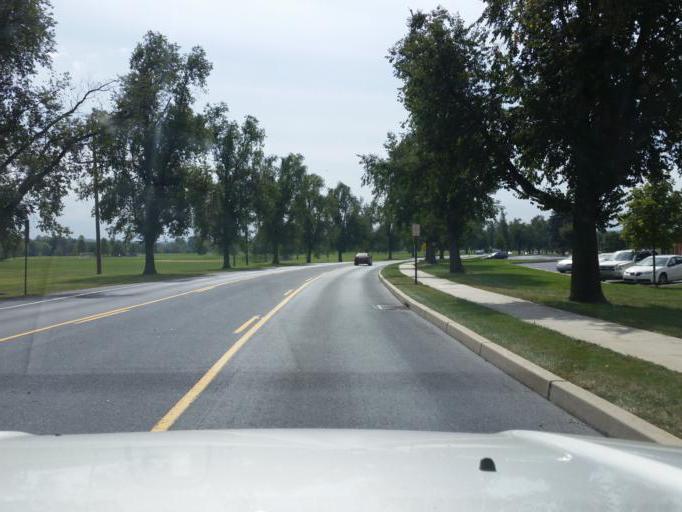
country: US
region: Pennsylvania
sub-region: Dauphin County
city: Hershey
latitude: 40.2806
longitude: -76.6402
